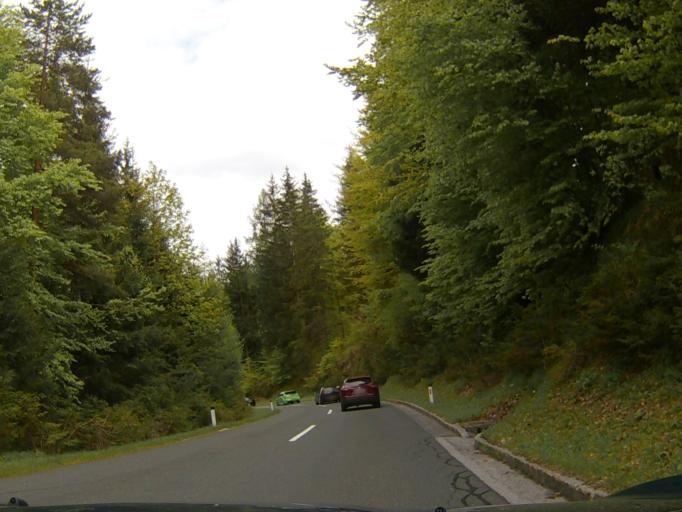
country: AT
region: Carinthia
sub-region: Villach Stadt
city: Villach
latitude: 46.5794
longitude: 13.7855
